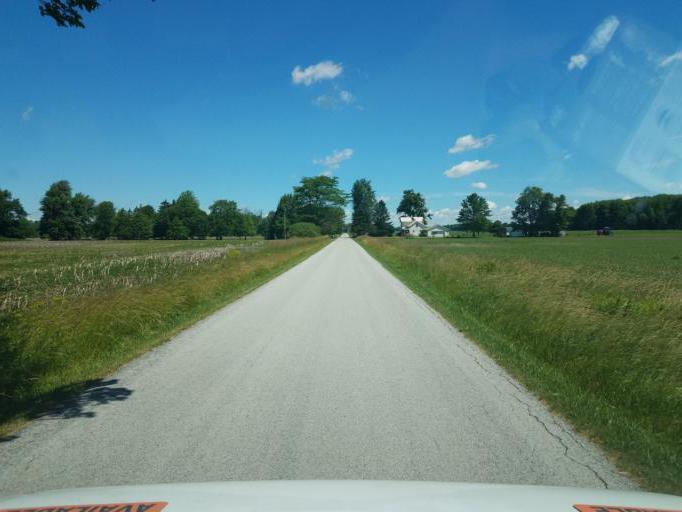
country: US
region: Ohio
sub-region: Morrow County
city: Cardington
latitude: 40.5470
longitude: -82.9482
